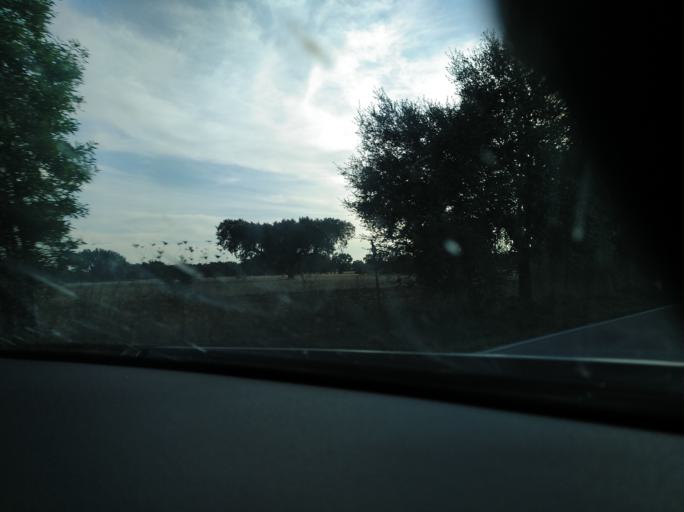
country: PT
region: Portalegre
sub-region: Fronteira
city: Fronteira
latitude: 38.9618
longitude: -7.5937
